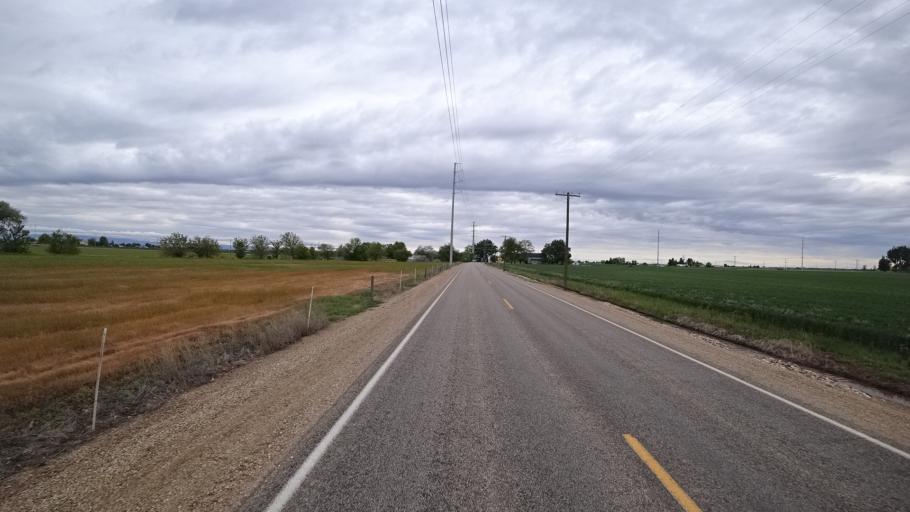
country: US
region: Idaho
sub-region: Ada County
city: Star
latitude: 43.6486
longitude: -116.5096
